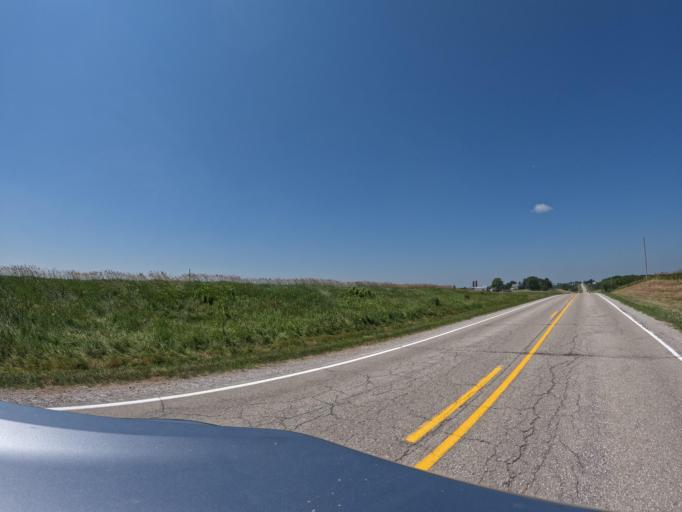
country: US
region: Iowa
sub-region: Keokuk County
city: Sigourney
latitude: 41.2649
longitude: -92.2111
